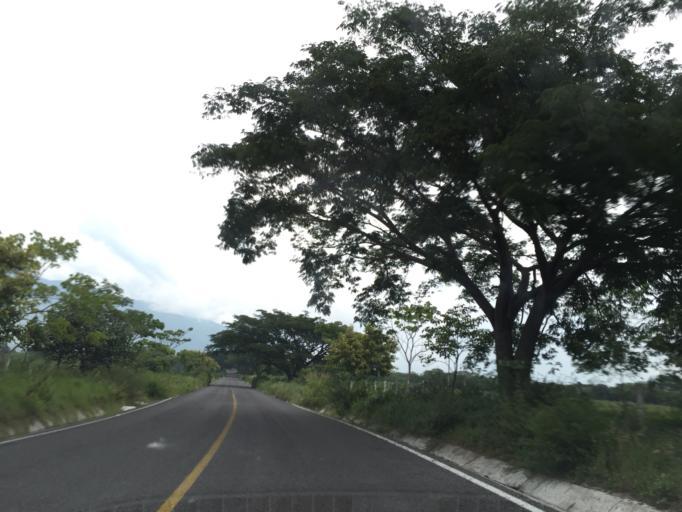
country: MX
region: Colima
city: Comala
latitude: 19.3513
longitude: -103.7897
